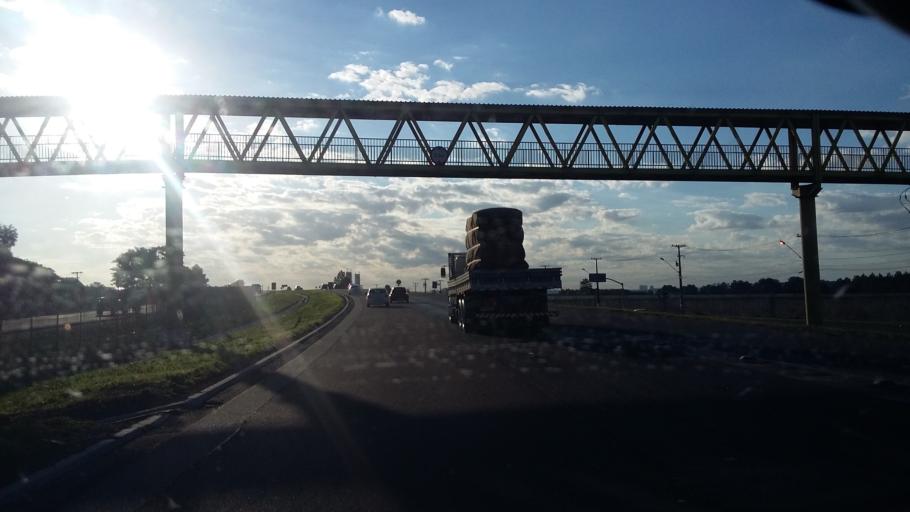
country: BR
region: Parana
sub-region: Sao Jose Dos Pinhais
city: Sao Jose dos Pinhais
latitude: -25.5367
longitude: -49.3142
